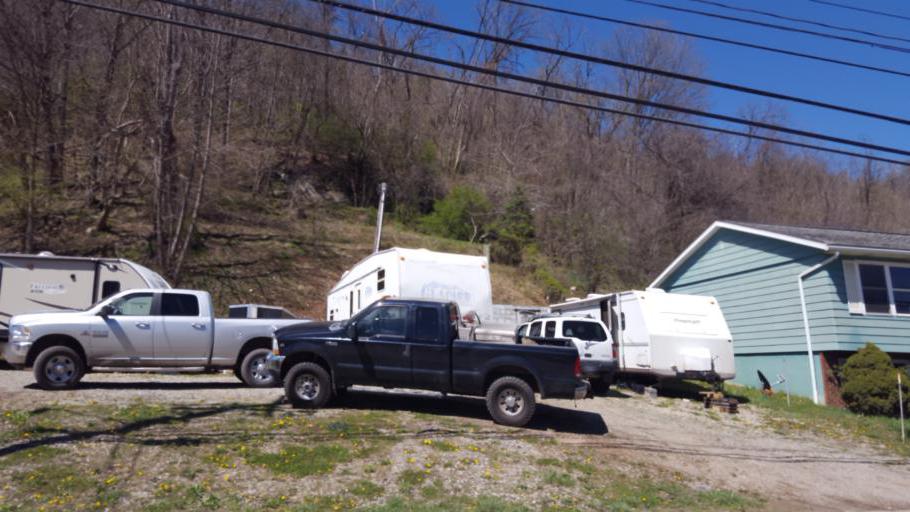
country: US
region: Ohio
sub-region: Belmont County
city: Wolfhurst
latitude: 40.0710
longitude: -80.8013
